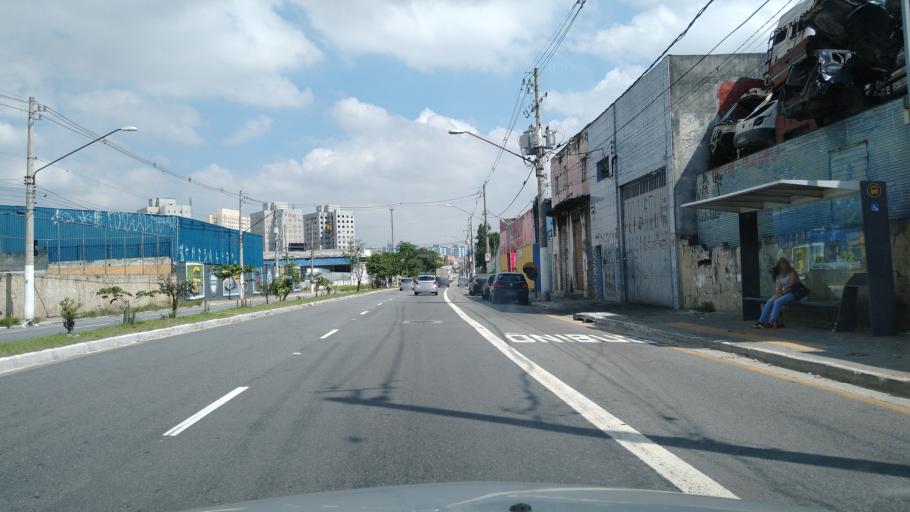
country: BR
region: Sao Paulo
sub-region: Guarulhos
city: Guarulhos
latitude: -23.4891
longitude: -46.5049
